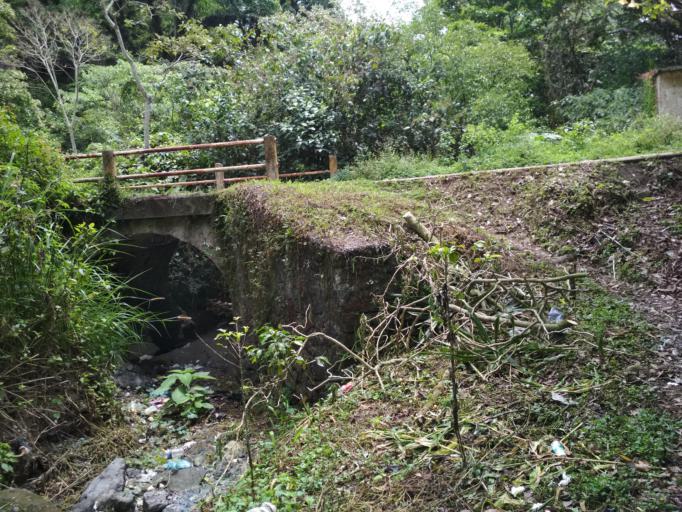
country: MX
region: Veracruz
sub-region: Jilotepec
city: El Pueblito (Garbanzal)
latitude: 19.6195
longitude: -96.9258
